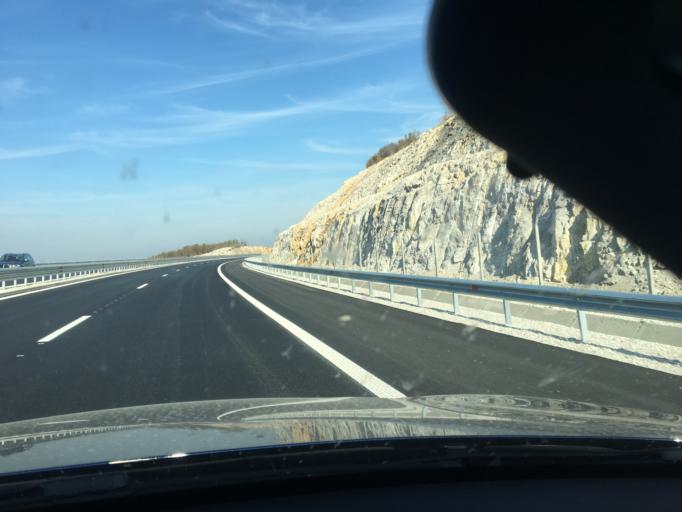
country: BG
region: Lovech
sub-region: Obshtina Yablanitsa
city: Yablanitsa
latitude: 43.0444
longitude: 24.1276
